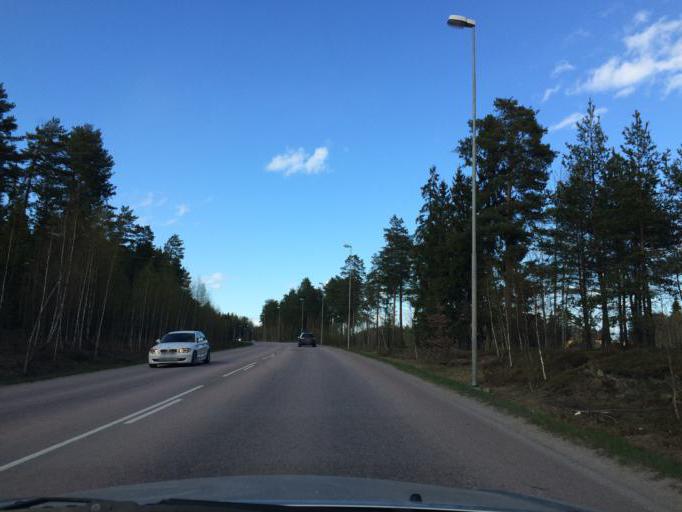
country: SE
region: Vaestmanland
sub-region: Vasteras
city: Vasteras
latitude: 59.6391
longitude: 16.5494
